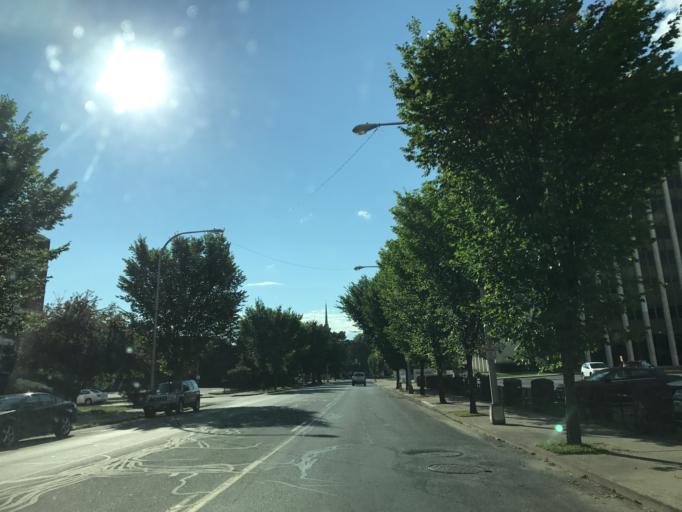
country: US
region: New York
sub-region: Warren County
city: Glens Falls
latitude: 43.3112
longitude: -73.6473
